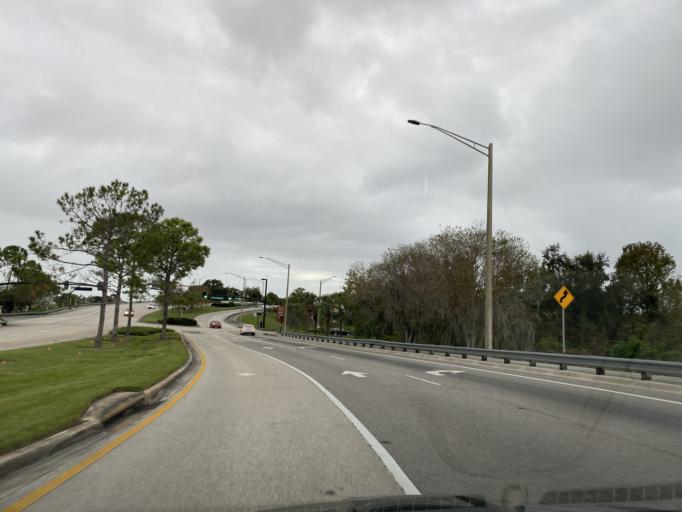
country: US
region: Florida
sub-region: Orange County
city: Belle Isle
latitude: 28.4432
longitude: -81.3083
